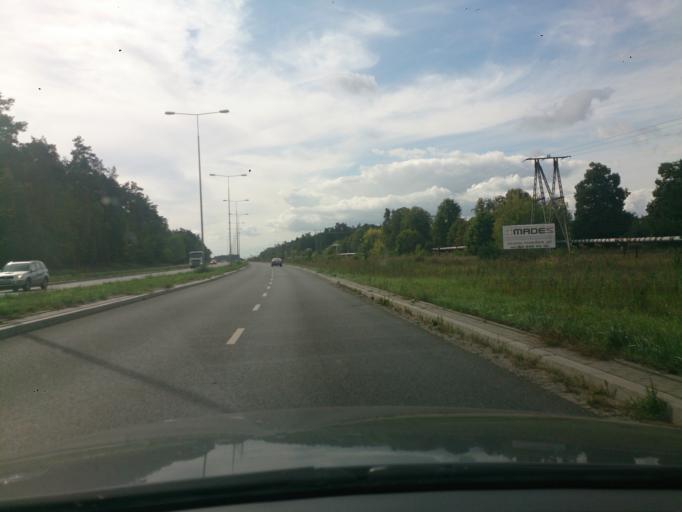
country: PL
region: Kujawsko-Pomorskie
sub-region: Grudziadz
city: Grudziadz
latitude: 53.4618
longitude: 18.7451
